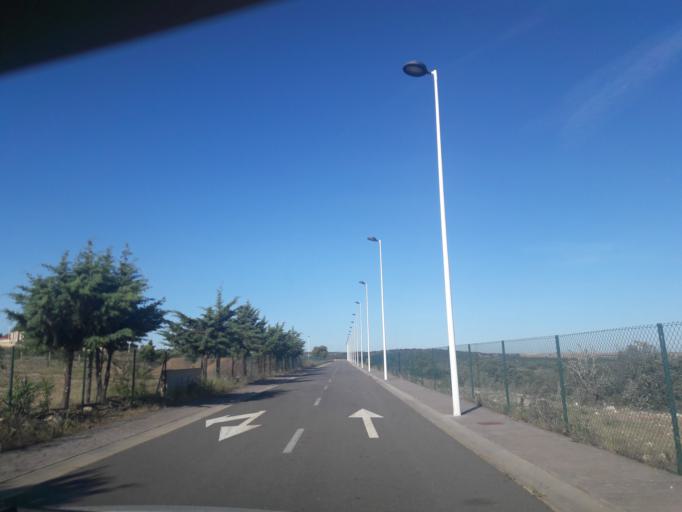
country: ES
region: Castille and Leon
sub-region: Provincia de Salamanca
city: Morille
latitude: 40.8076
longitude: -5.6497
